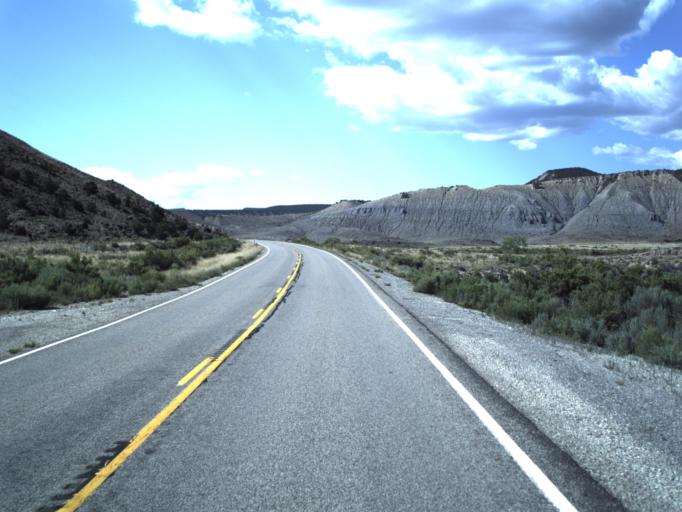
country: US
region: Utah
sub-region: Emery County
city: Ferron
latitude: 38.7886
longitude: -111.3495
